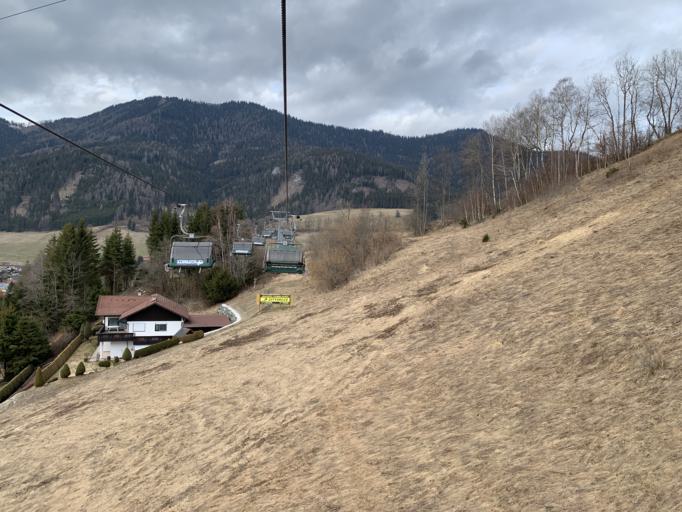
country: AT
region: Styria
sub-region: Politischer Bezirk Bruck-Muerzzuschlag
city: Spital am Semmering
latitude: 47.6104
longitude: 15.7589
